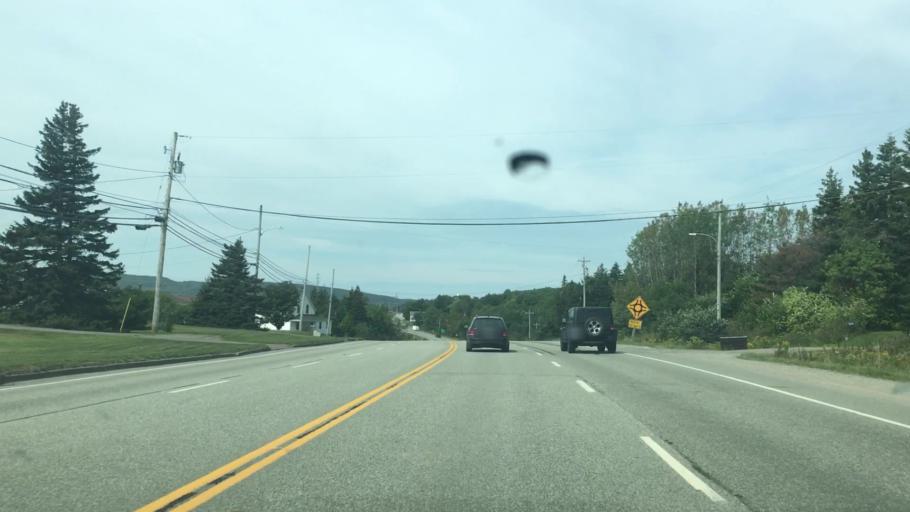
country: CA
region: Nova Scotia
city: Port Hawkesbury
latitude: 45.6424
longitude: -61.3919
